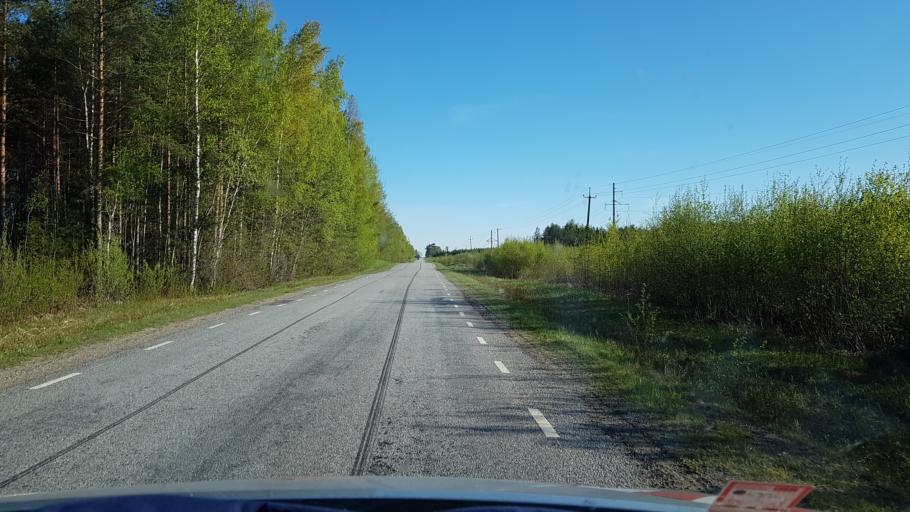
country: EE
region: Vorumaa
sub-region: Voru linn
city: Voru
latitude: 57.9362
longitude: 26.9526
